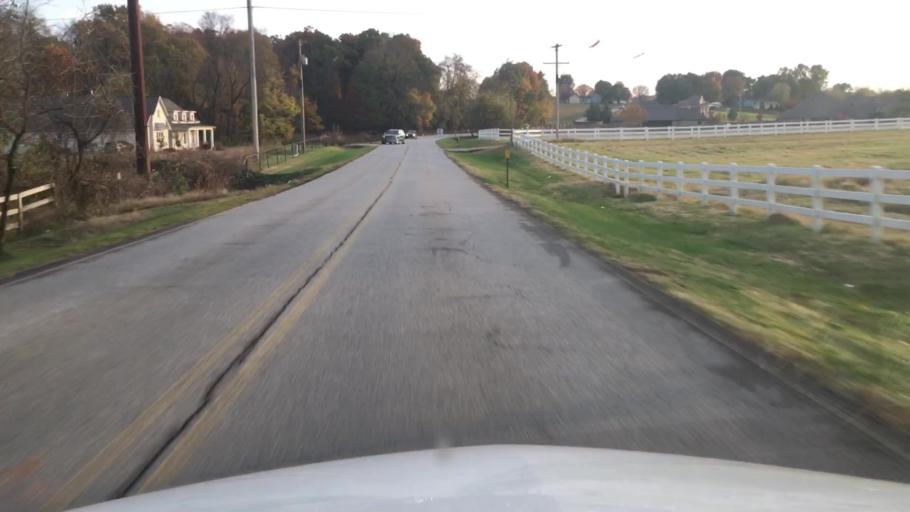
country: US
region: Arkansas
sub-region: Washington County
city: Tontitown
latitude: 36.1894
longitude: -94.2316
